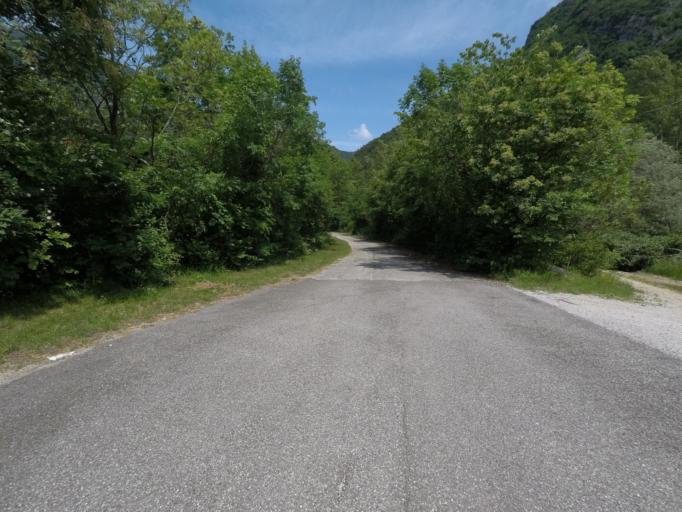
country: IT
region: Friuli Venezia Giulia
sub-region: Provincia di Udine
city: Amaro
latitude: 46.3802
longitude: 13.1373
